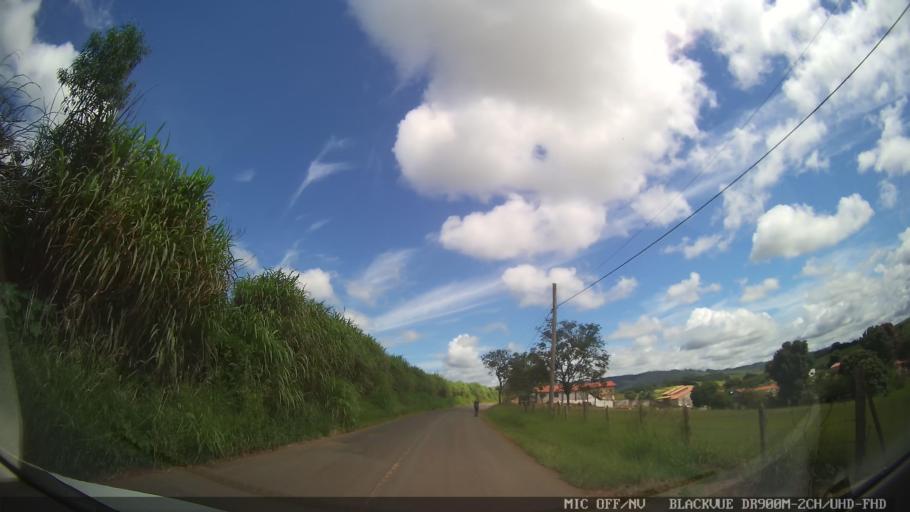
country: BR
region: Sao Paulo
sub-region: Amparo
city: Amparo
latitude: -22.8615
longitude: -46.7087
